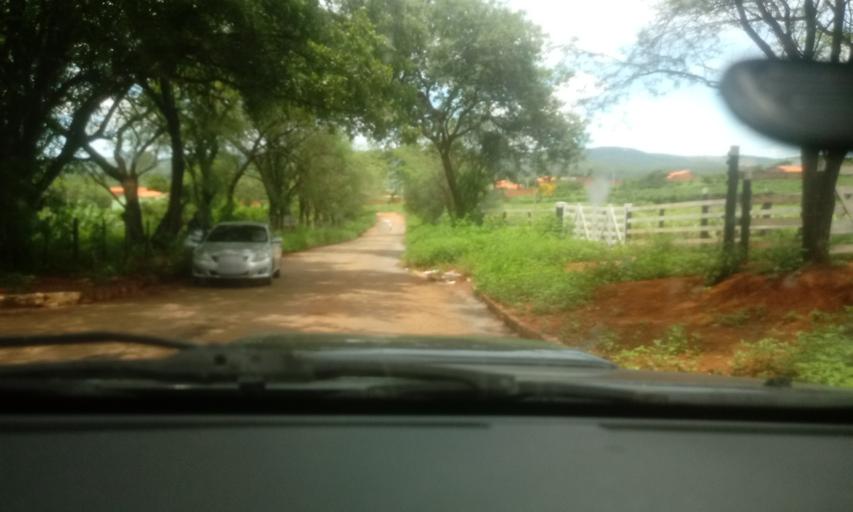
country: BR
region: Bahia
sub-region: Riacho De Santana
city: Riacho de Santana
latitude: -13.6028
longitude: -42.9465
